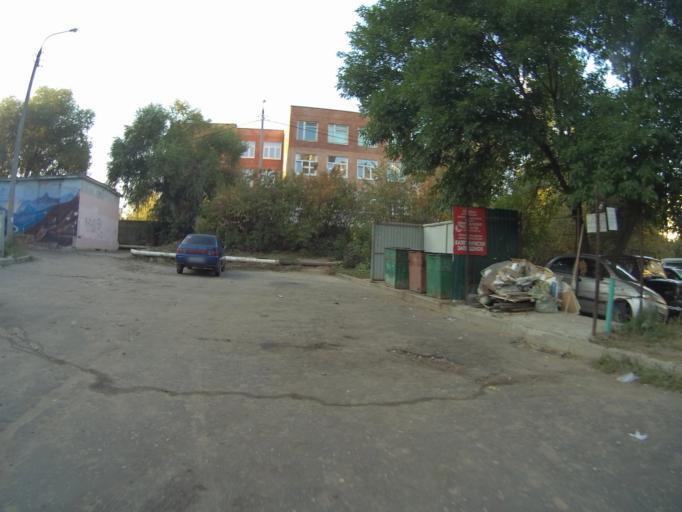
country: RU
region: Vladimir
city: Vladimir
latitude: 56.1066
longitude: 40.3503
